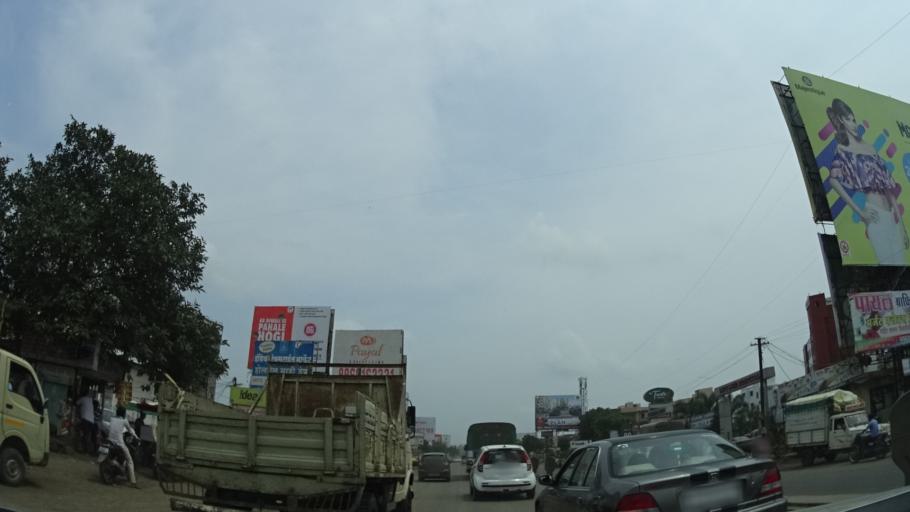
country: IN
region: Maharashtra
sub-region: Pune Division
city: Lohogaon
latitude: 18.5828
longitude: 73.9888
